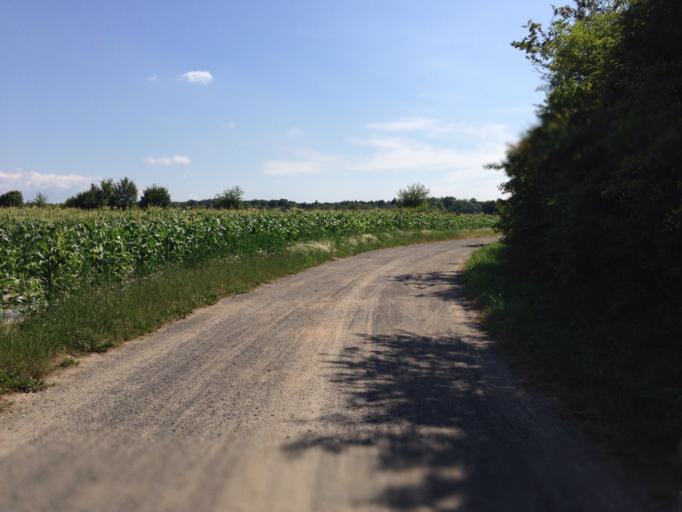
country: DE
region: Hesse
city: Bruchkobel
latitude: 50.1626
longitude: 8.9101
